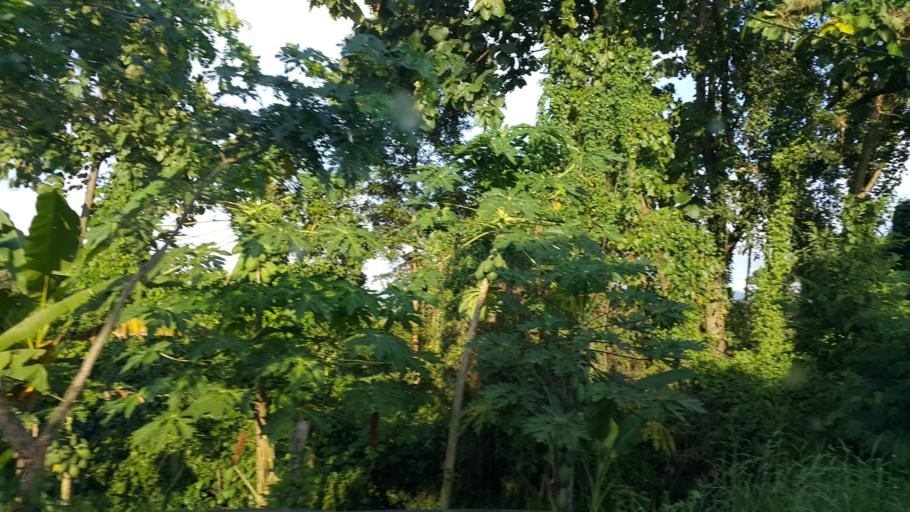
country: TH
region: Chiang Mai
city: Mae On
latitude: 18.7434
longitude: 99.2364
